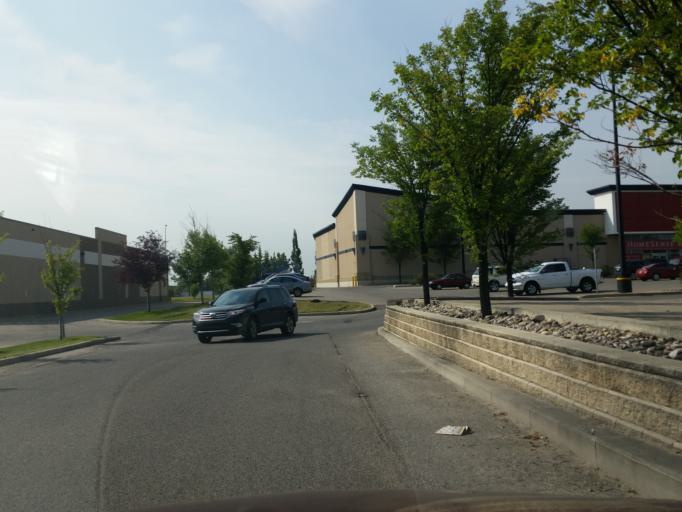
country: CA
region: Alberta
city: Calgary
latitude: 51.0688
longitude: -113.9894
